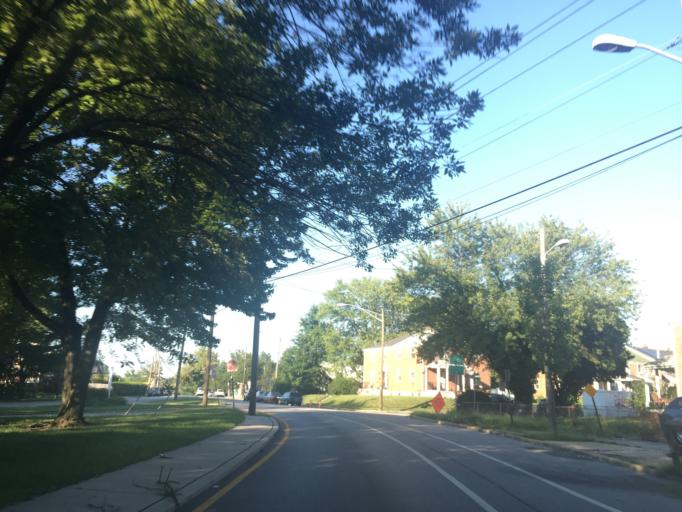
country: US
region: Maryland
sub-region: Baltimore County
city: Charlestown
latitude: 39.2885
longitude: -76.7100
